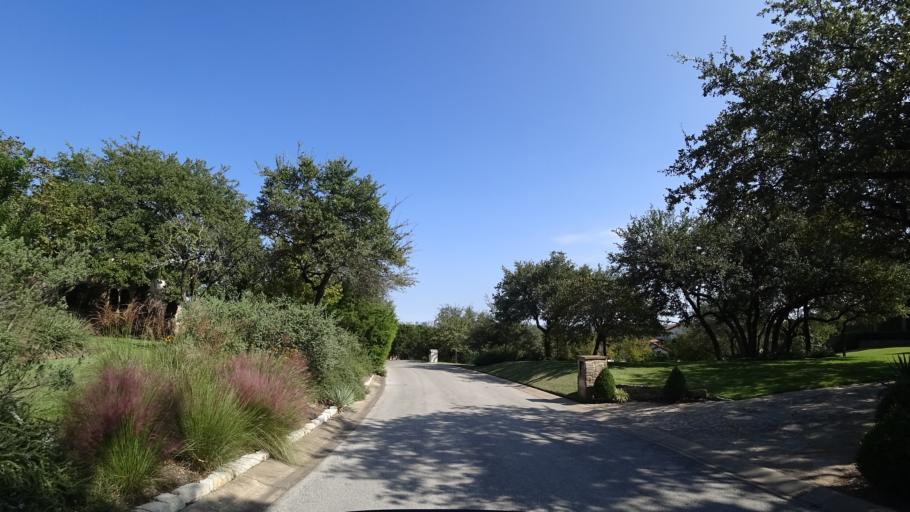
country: US
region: Texas
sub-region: Travis County
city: West Lake Hills
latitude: 30.2879
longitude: -97.8072
